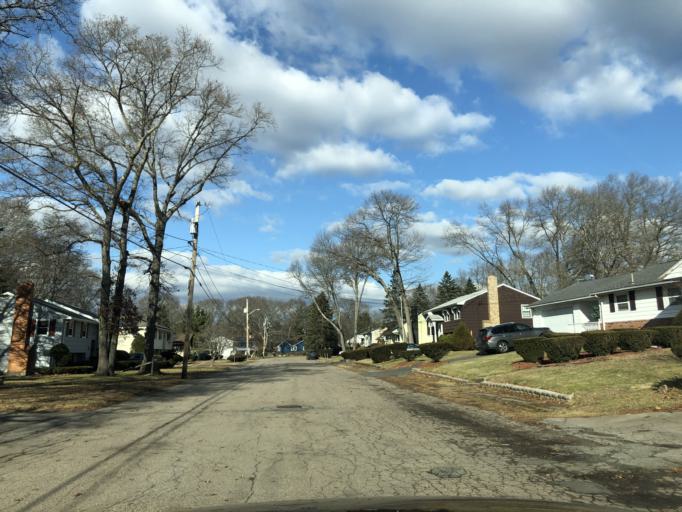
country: US
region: Massachusetts
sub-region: Plymouth County
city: Brockton
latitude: 42.1052
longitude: -71.0077
